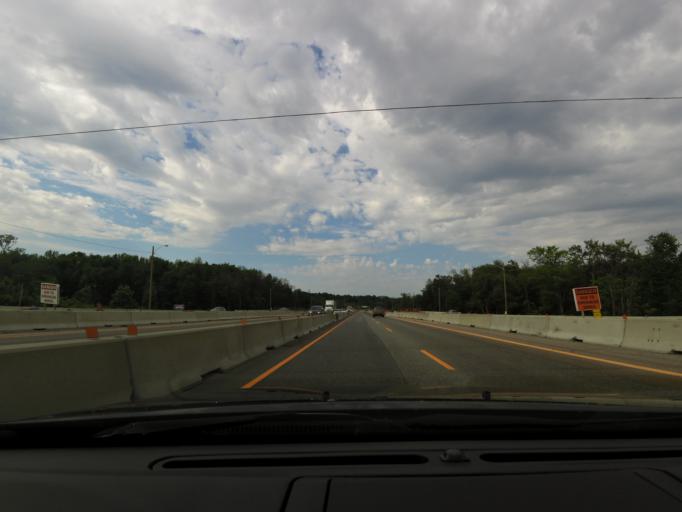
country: CA
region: Ontario
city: Barrie
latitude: 44.4257
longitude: -79.6522
